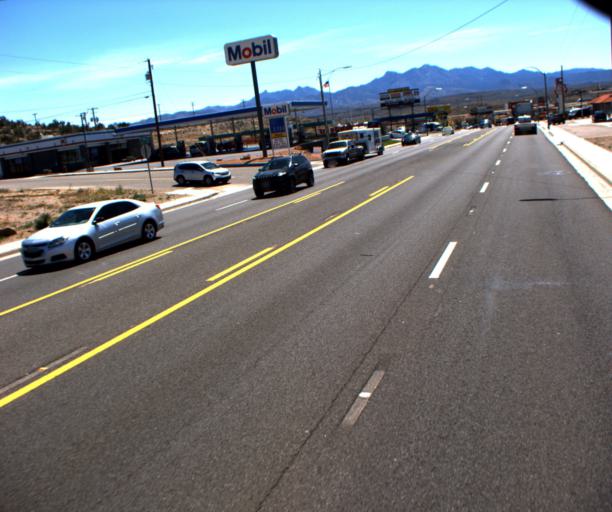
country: US
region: Arizona
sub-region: Mohave County
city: Kingman
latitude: 35.1936
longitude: -114.0723
